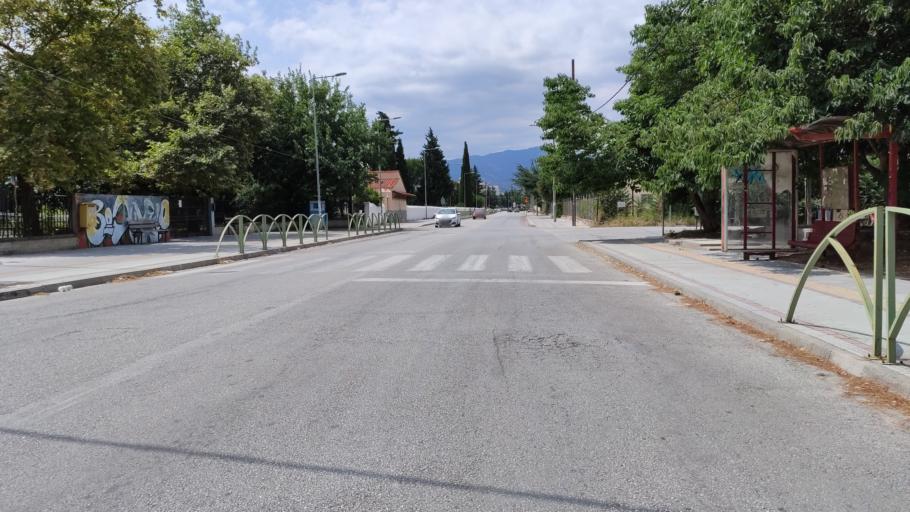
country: GR
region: East Macedonia and Thrace
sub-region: Nomos Rodopis
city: Komotini
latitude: 41.1225
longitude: 25.3979
